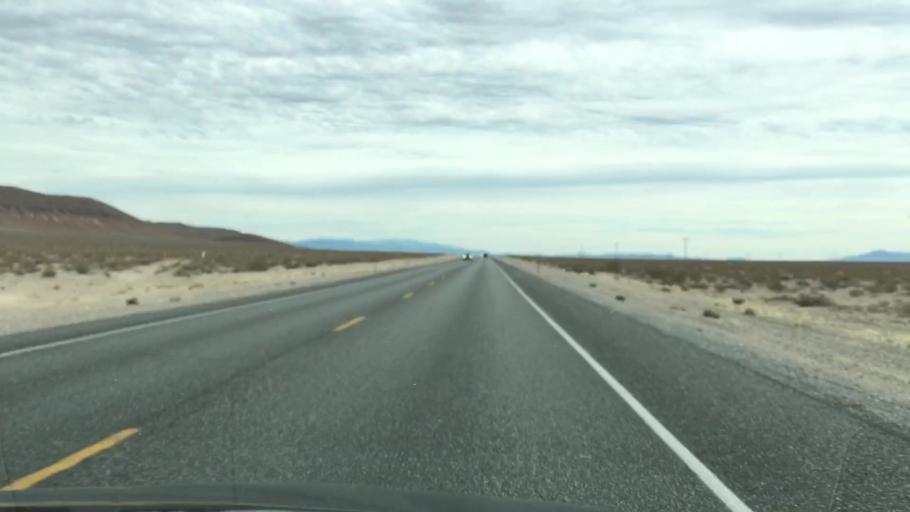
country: US
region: Nevada
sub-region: Nye County
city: Beatty
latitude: 36.7049
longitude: -116.5895
